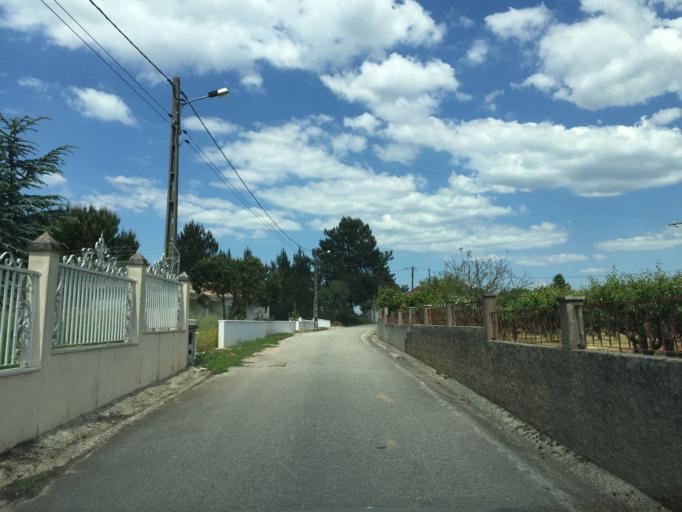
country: PT
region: Santarem
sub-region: Ourem
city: Ourem
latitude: 39.6788
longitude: -8.5684
